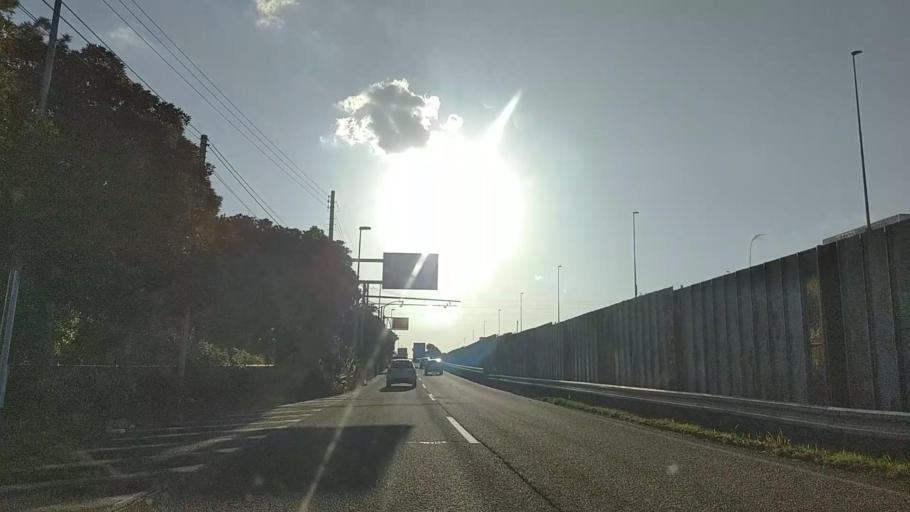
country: JP
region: Tokyo
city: Urayasu
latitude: 35.6603
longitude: 139.9157
